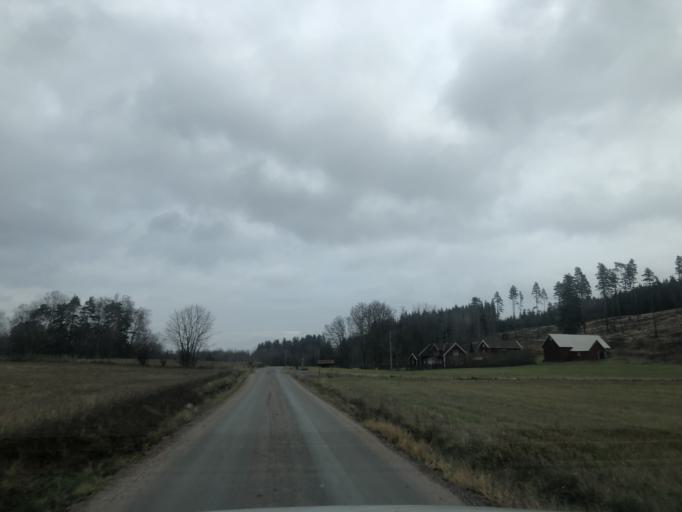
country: SE
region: Vaestra Goetaland
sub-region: Ulricehamns Kommun
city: Ulricehamn
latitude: 57.8900
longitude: 13.4684
